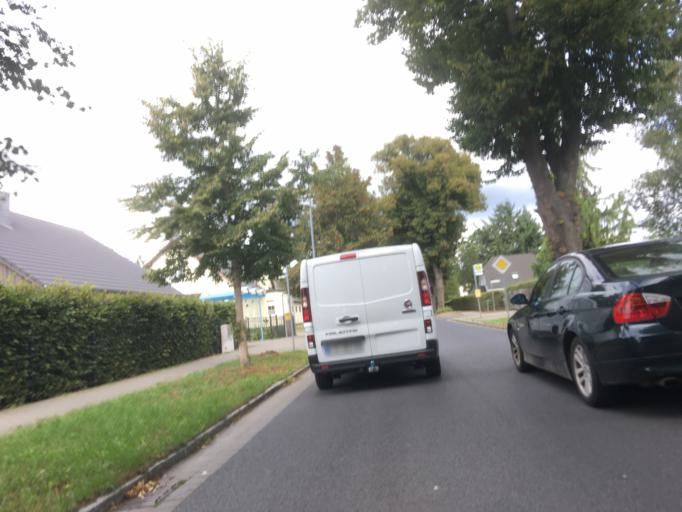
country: DE
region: Brandenburg
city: Konigs Wusterhausen
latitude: 52.3066
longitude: 13.7021
